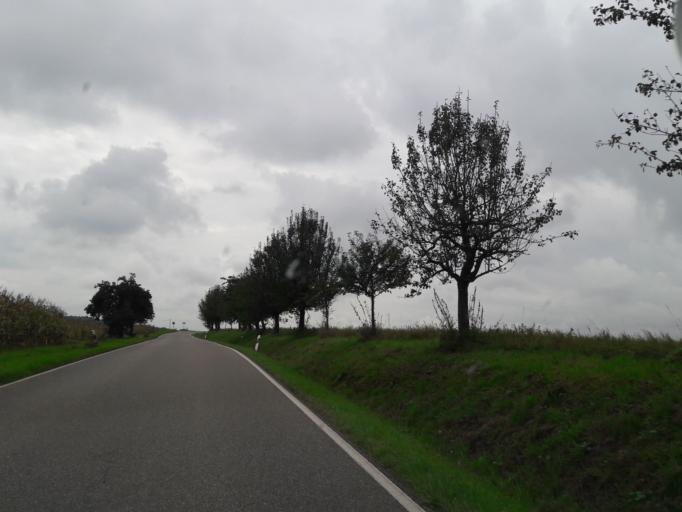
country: DE
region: Baden-Wuerttemberg
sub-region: Regierungsbezirk Stuttgart
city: Neuenstadt am Kocher
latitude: 49.2185
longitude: 9.2996
